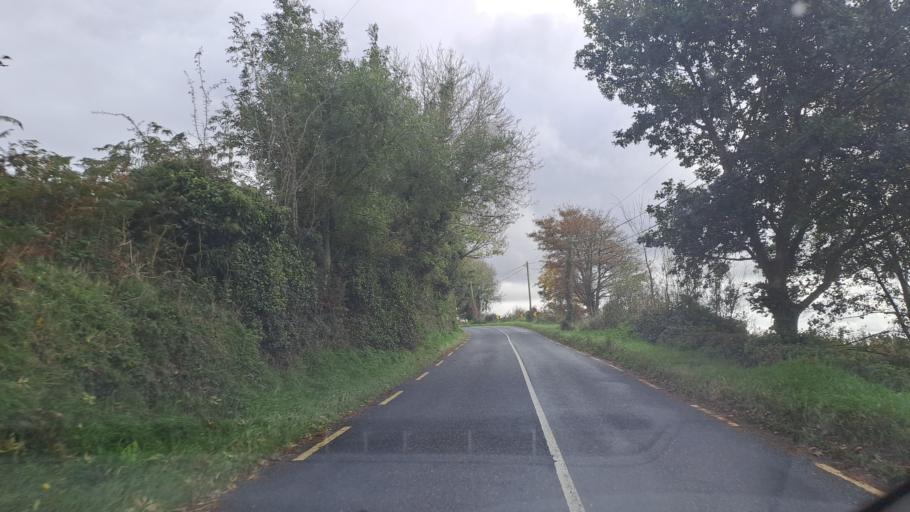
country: IE
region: Ulster
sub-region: An Cabhan
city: Virginia
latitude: 53.8334
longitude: -7.0402
